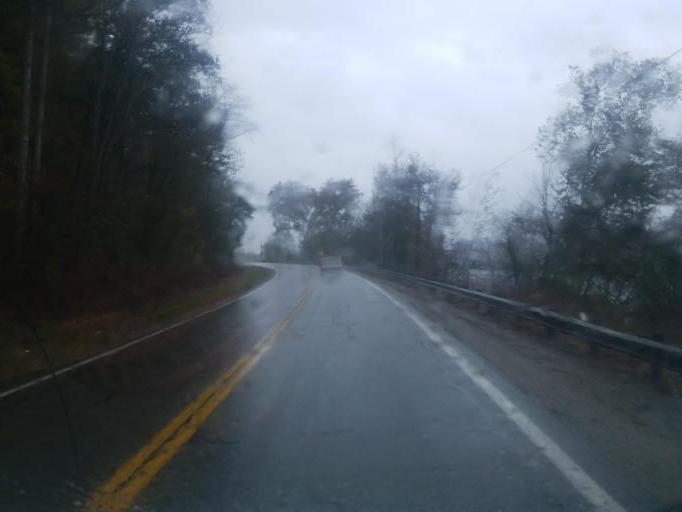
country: US
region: Ohio
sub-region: Muskingum County
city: Pleasant Grove
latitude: 39.8527
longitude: -81.8995
